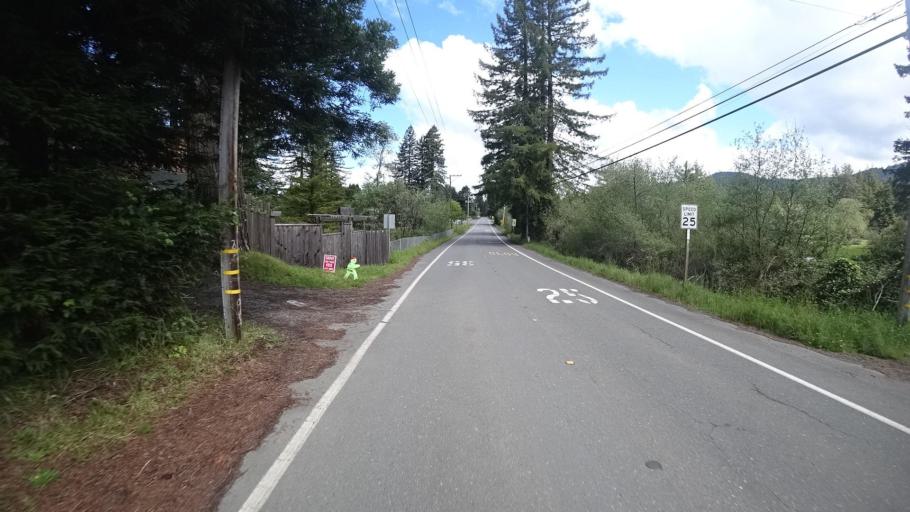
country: US
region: California
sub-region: Humboldt County
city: McKinleyville
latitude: 40.9544
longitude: -124.0337
